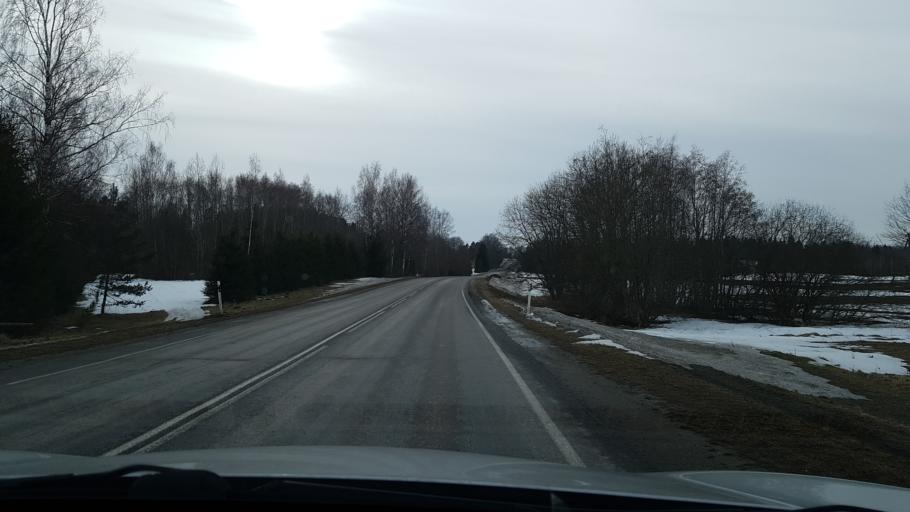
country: EE
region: Tartu
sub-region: Noo vald
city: Noo
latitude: 58.2264
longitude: 26.6381
